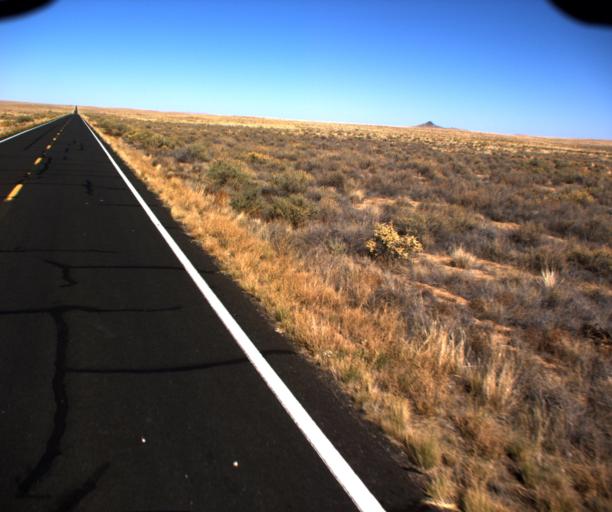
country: US
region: Arizona
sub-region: Navajo County
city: Dilkon
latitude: 35.5797
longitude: -110.4634
